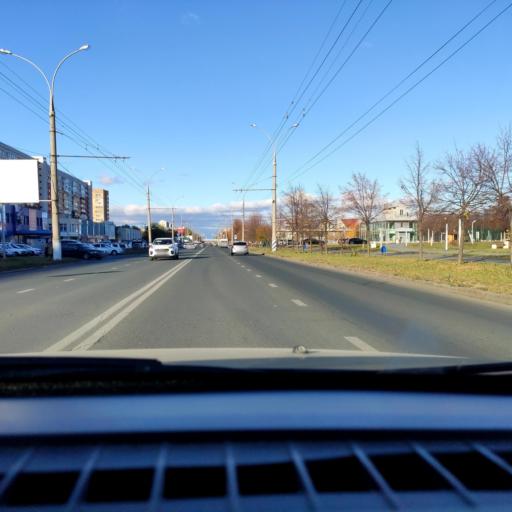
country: RU
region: Samara
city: Tol'yatti
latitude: 53.5112
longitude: 49.2717
